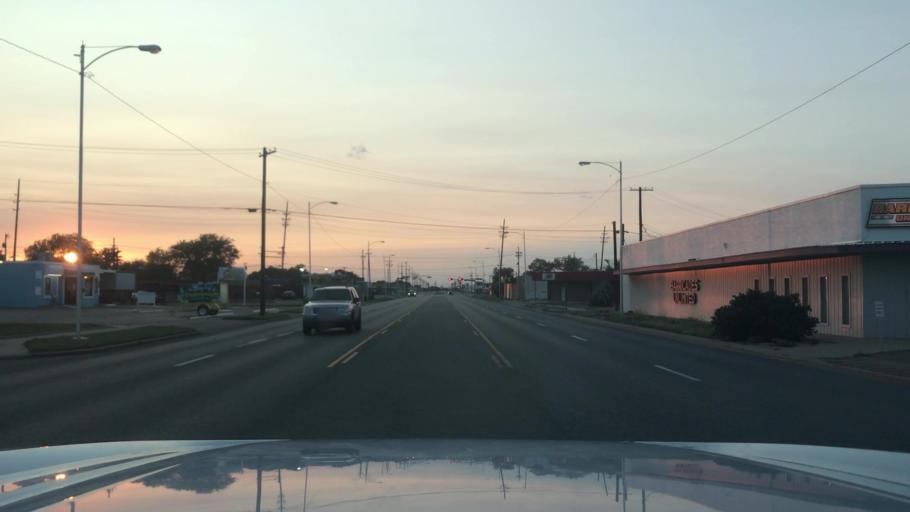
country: US
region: Texas
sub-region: Lubbock County
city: Lubbock
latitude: 33.5979
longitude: -101.8596
